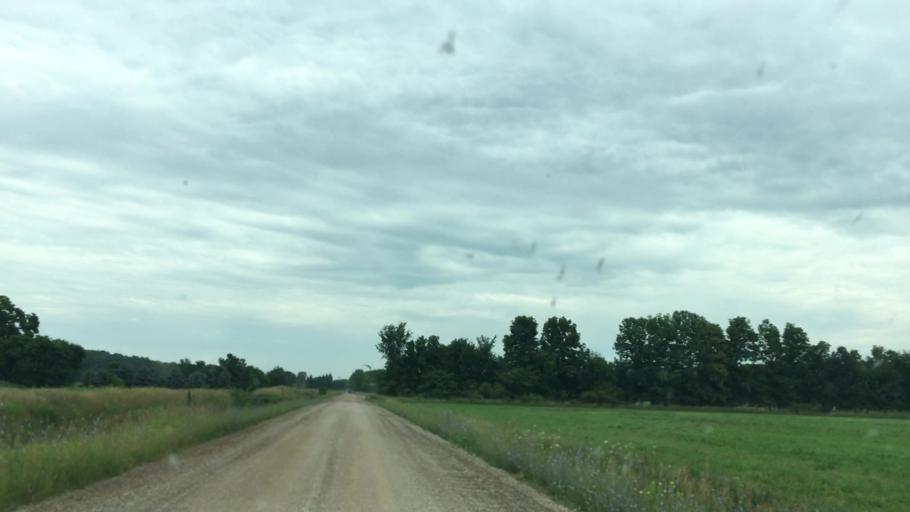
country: US
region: Michigan
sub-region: Clinton County
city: Saint Johns
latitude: 43.0803
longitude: -84.4839
